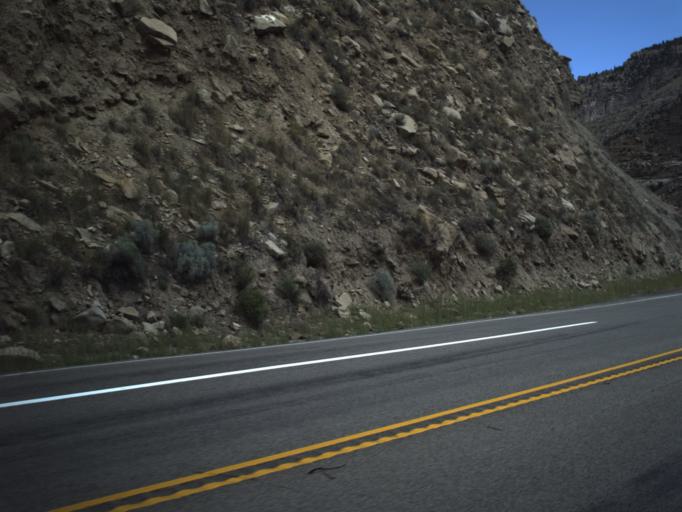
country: US
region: Utah
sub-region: Carbon County
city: Helper
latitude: 39.7201
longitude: -110.8658
